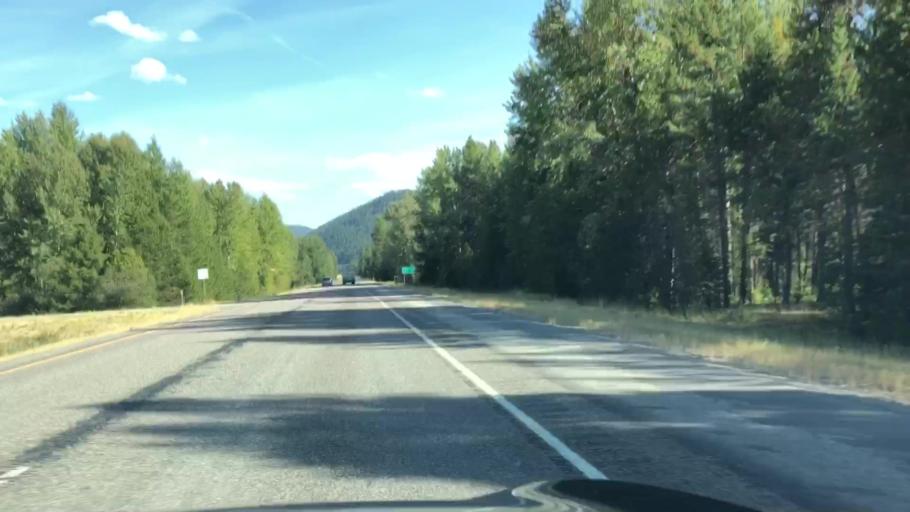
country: US
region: Montana
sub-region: Sanders County
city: Thompson Falls
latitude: 47.3697
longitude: -115.3377
